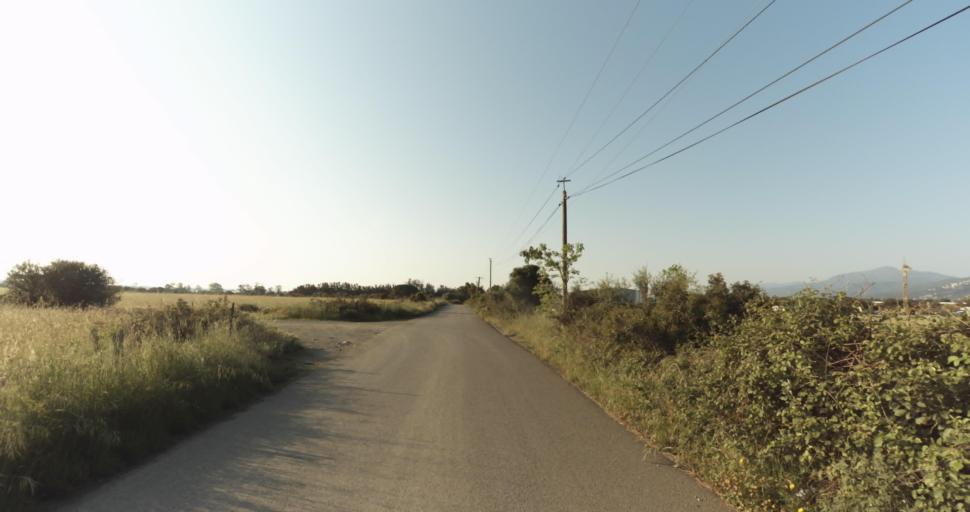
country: FR
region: Corsica
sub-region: Departement de la Haute-Corse
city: Biguglia
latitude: 42.6059
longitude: 9.4515
